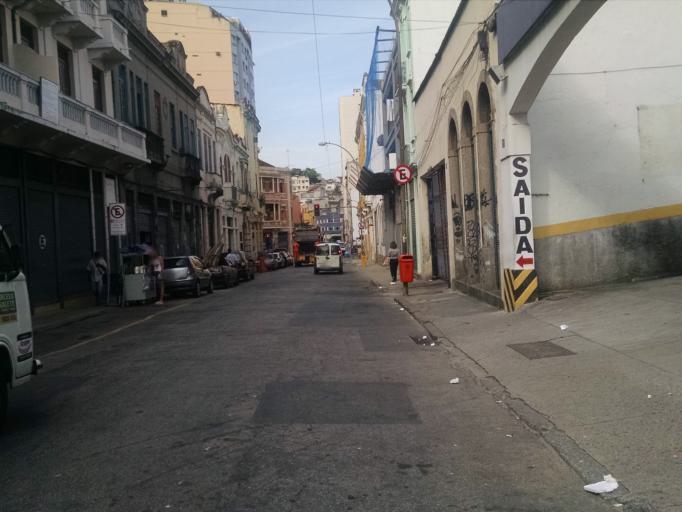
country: BR
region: Rio de Janeiro
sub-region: Rio De Janeiro
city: Rio de Janeiro
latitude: -22.9110
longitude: -43.1903
